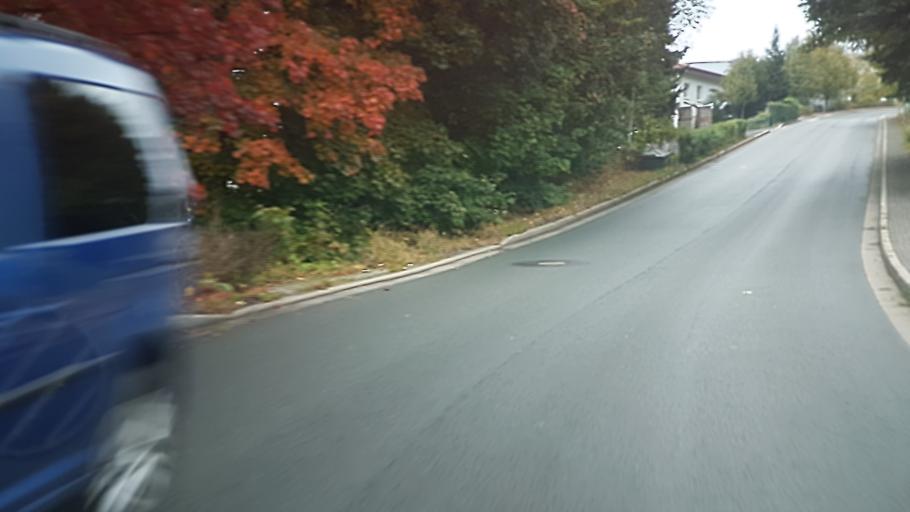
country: DE
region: North Rhine-Westphalia
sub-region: Regierungsbezirk Arnsberg
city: Luedenscheid
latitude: 51.2100
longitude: 7.6635
